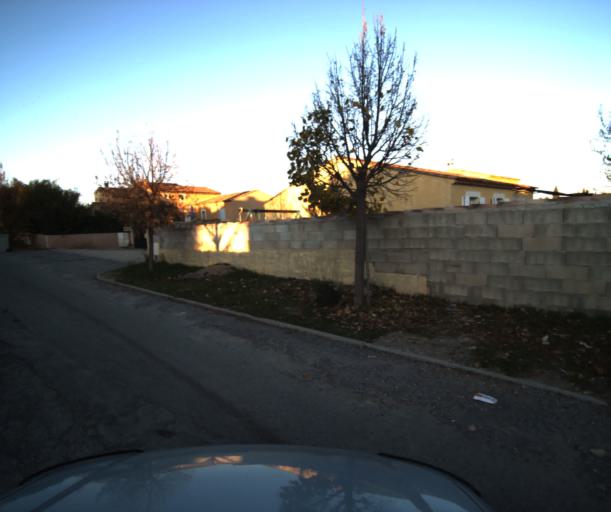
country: FR
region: Provence-Alpes-Cote d'Azur
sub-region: Departement du Vaucluse
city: Pertuis
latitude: 43.7013
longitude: 5.4979
